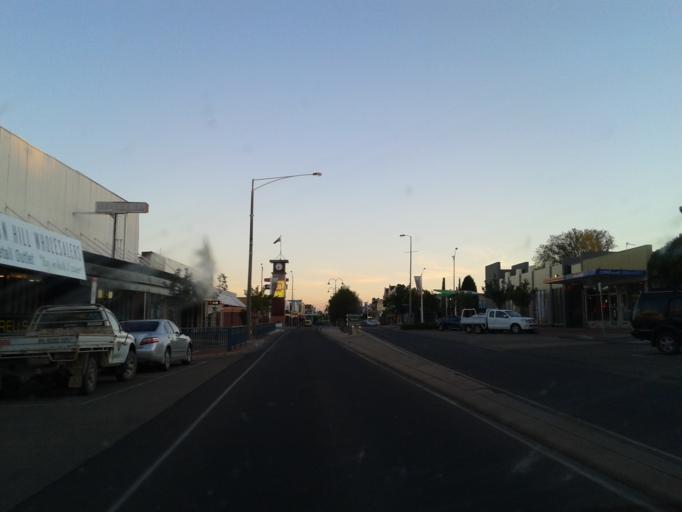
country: AU
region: Victoria
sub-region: Swan Hill
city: Swan Hill
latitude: -35.3375
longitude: 143.5592
